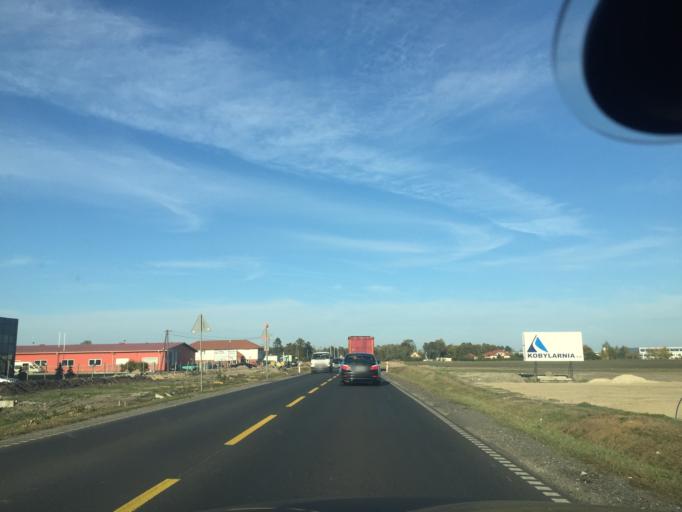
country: PL
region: Kujawsko-Pomorskie
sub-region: Powiat inowroclawski
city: Inowroclaw
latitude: 52.8220
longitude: 18.2993
